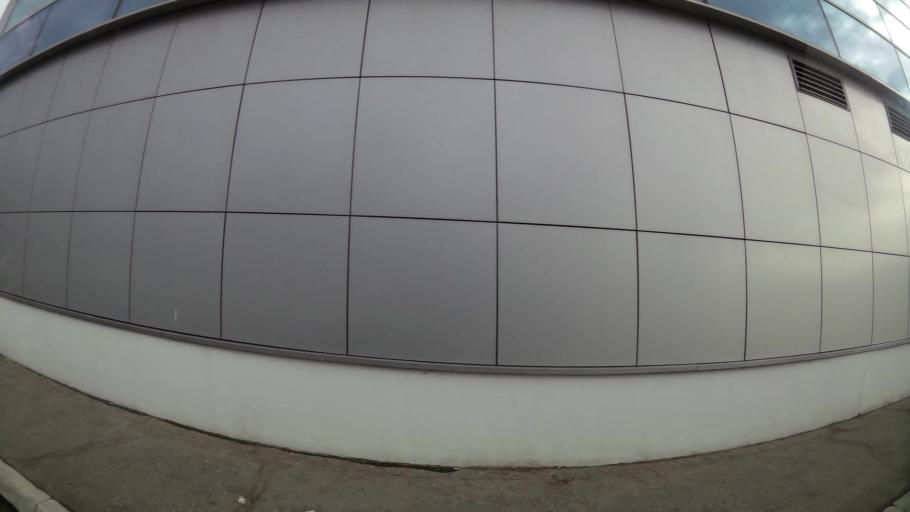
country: RS
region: Central Serbia
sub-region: Belgrade
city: Surcin
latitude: 44.8212
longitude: 20.2906
